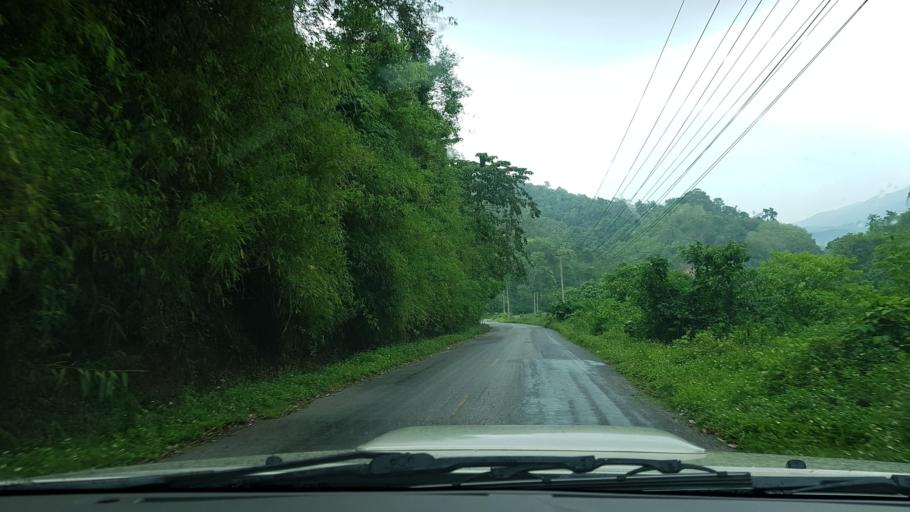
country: LA
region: Oudomxai
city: Muang Xay
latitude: 20.6147
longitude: 101.9518
